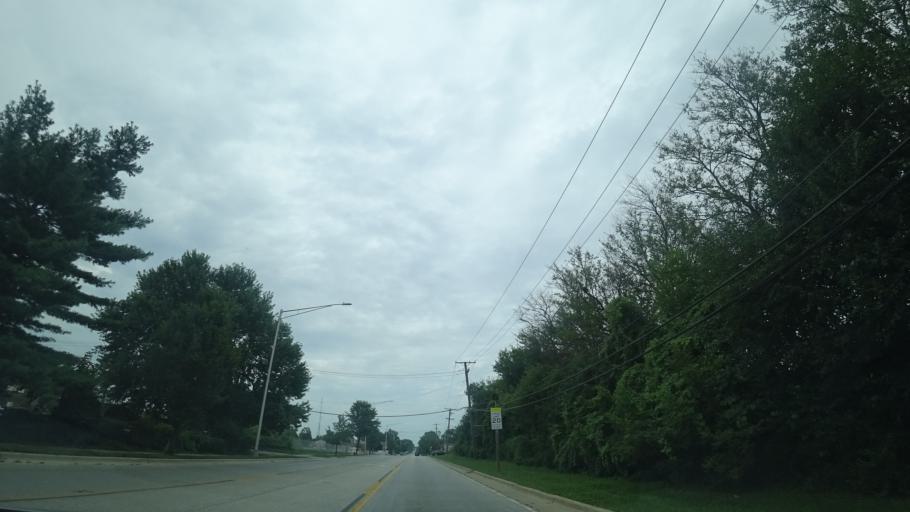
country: US
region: Illinois
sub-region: Cook County
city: Alsip
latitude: 41.6691
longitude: -87.7352
